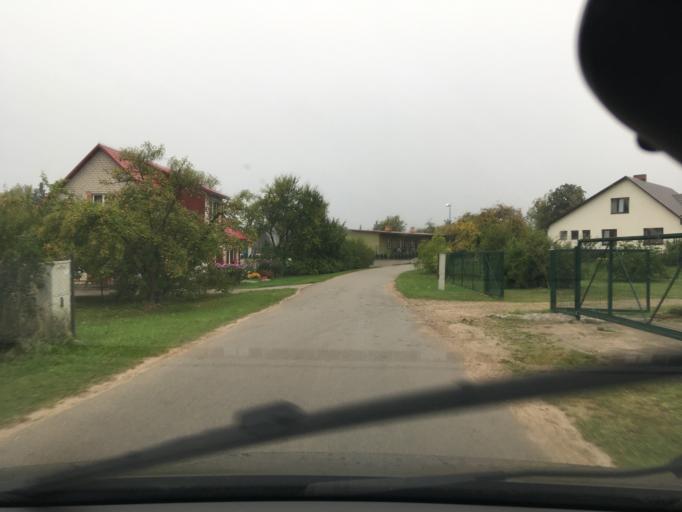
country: LV
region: Kuldigas Rajons
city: Kuldiga
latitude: 56.9881
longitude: 22.0217
